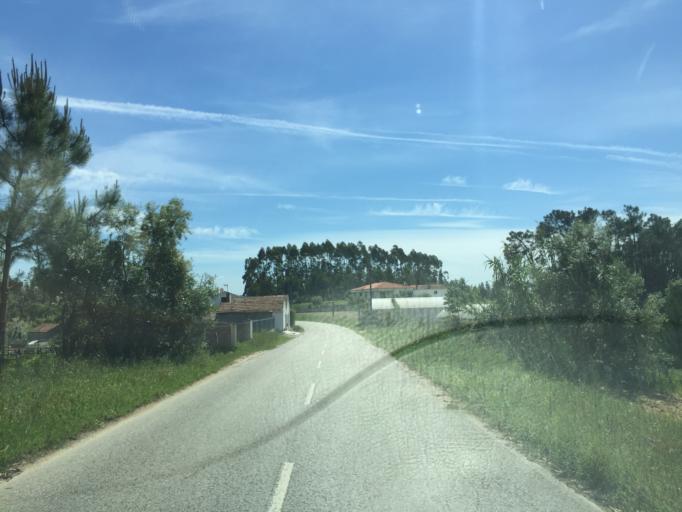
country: PT
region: Coimbra
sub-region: Figueira da Foz
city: Lavos
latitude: 40.0714
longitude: -8.7705
